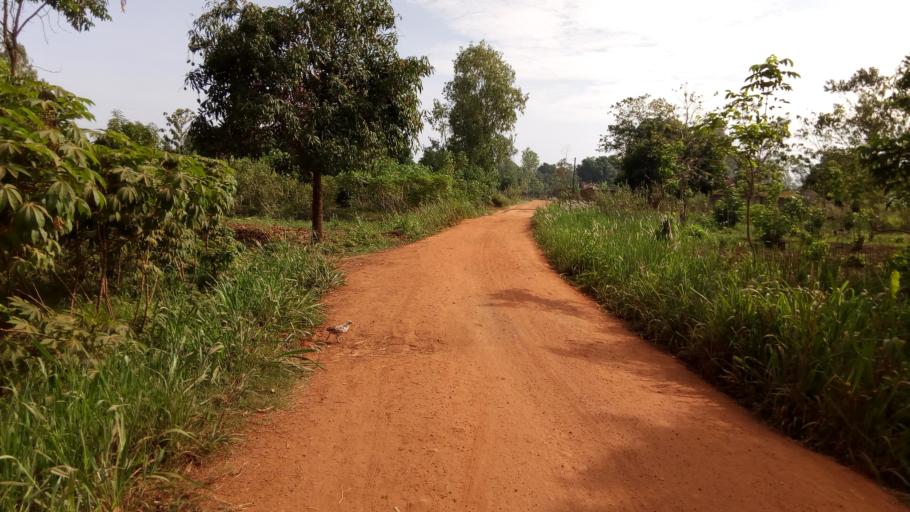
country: UG
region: Northern Region
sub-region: Gulu District
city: Gulu
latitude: 2.8025
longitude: 32.3227
